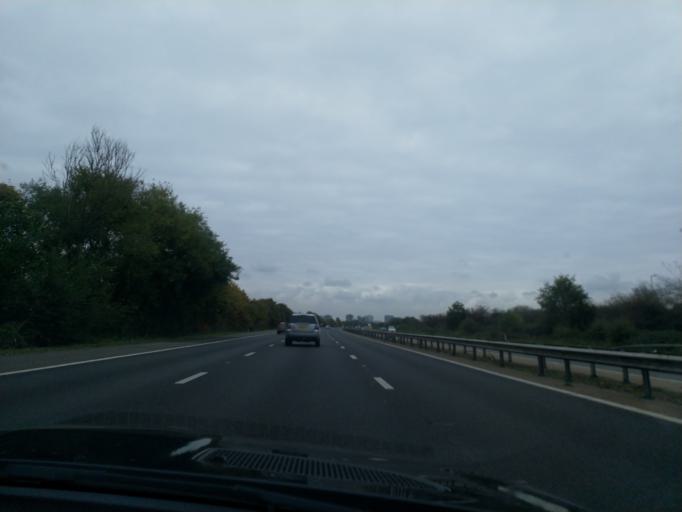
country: GB
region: England
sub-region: Surrey
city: Shepperton
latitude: 51.4073
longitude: -0.4430
